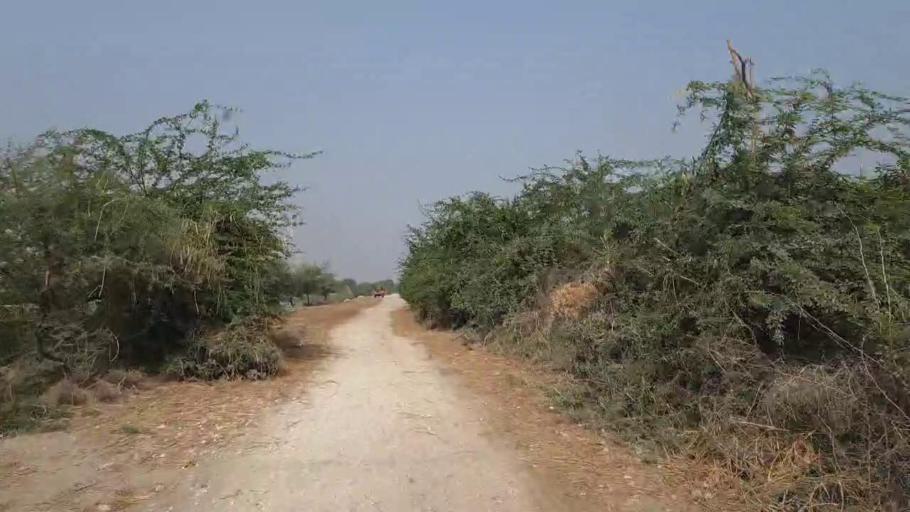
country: PK
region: Sindh
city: Kario
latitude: 24.9318
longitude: 68.6007
